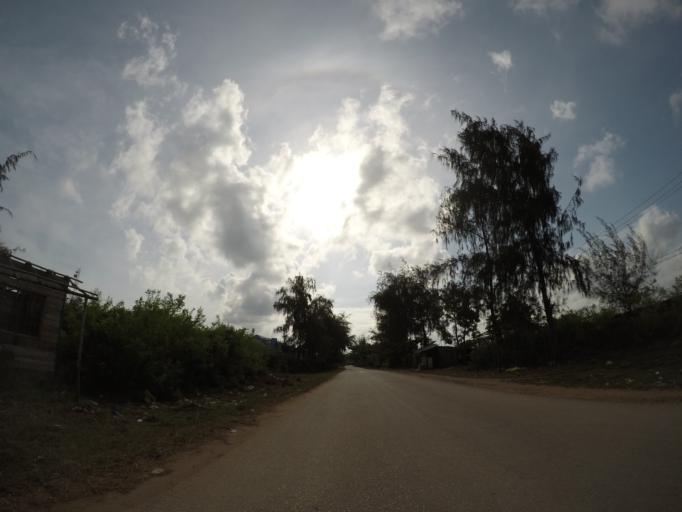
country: TZ
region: Zanzibar Central/South
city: Koani
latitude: -6.2257
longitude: 39.3180
